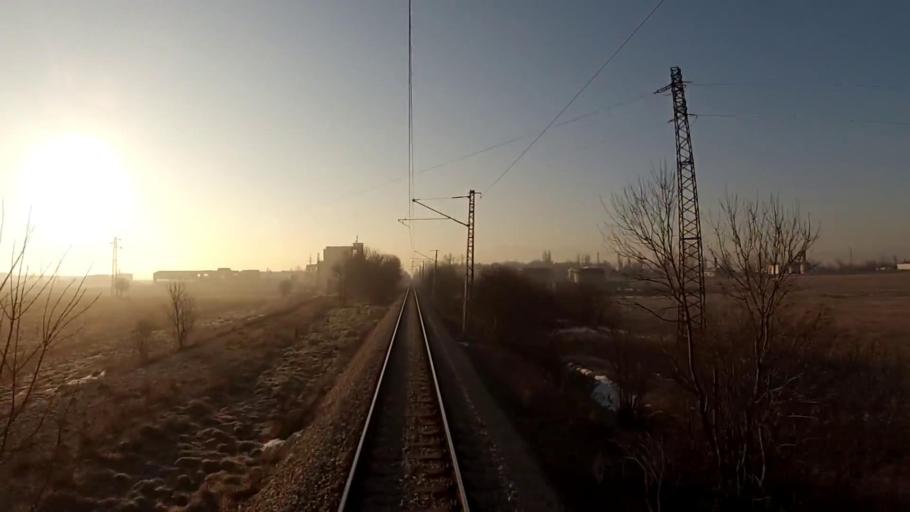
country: BG
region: Sofiya
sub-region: Obshtina Kostinbrod
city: Kostinbrod
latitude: 42.7922
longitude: 23.2097
